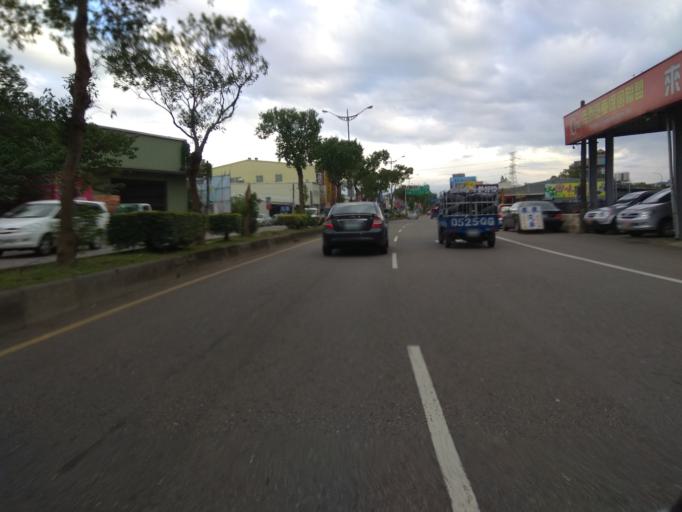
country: TW
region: Taiwan
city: Daxi
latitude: 24.8742
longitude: 121.2136
